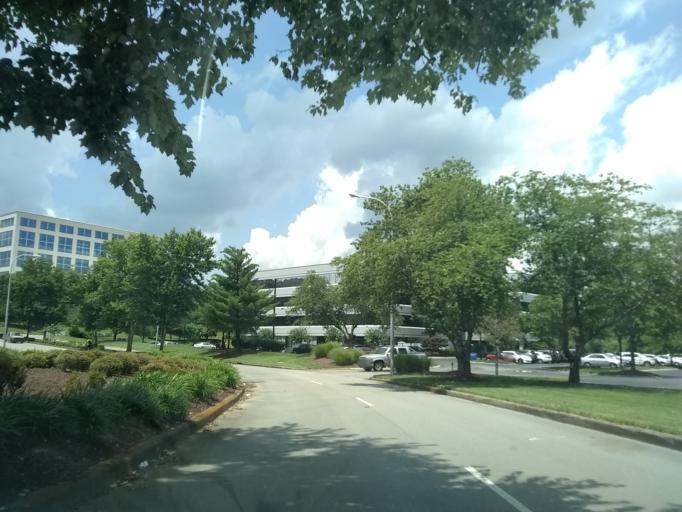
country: US
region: Tennessee
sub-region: Davidson County
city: Nashville
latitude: 36.1481
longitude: -86.6823
